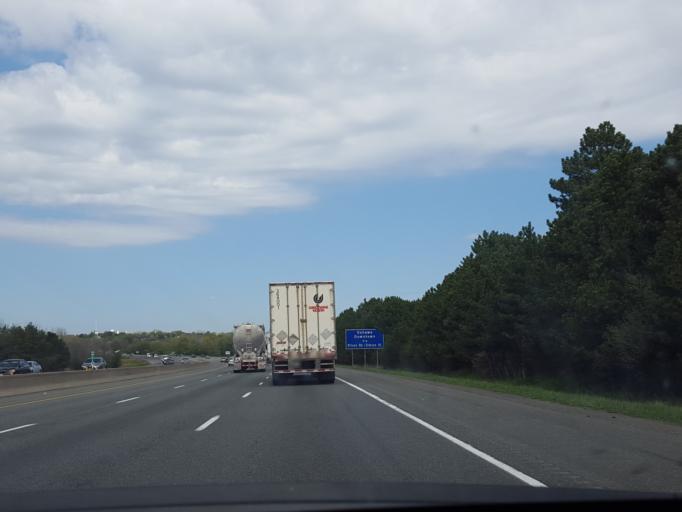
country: CA
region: Ontario
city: Oshawa
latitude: 43.8828
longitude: -78.8090
